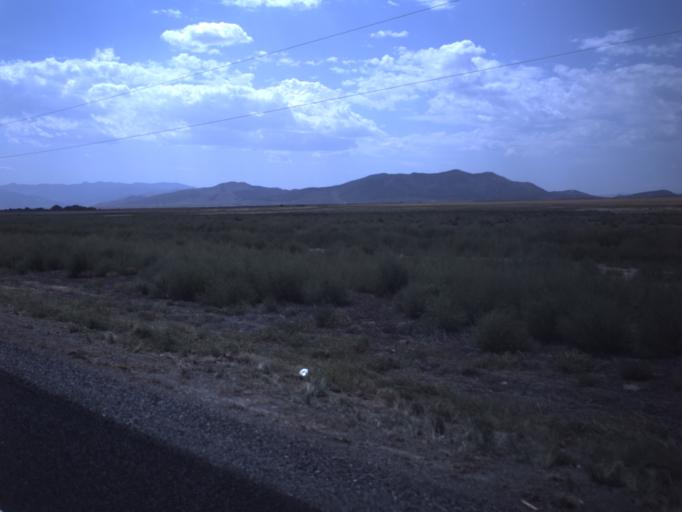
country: US
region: Utah
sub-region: Utah County
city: Eagle Mountain
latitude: 40.2810
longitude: -112.0956
